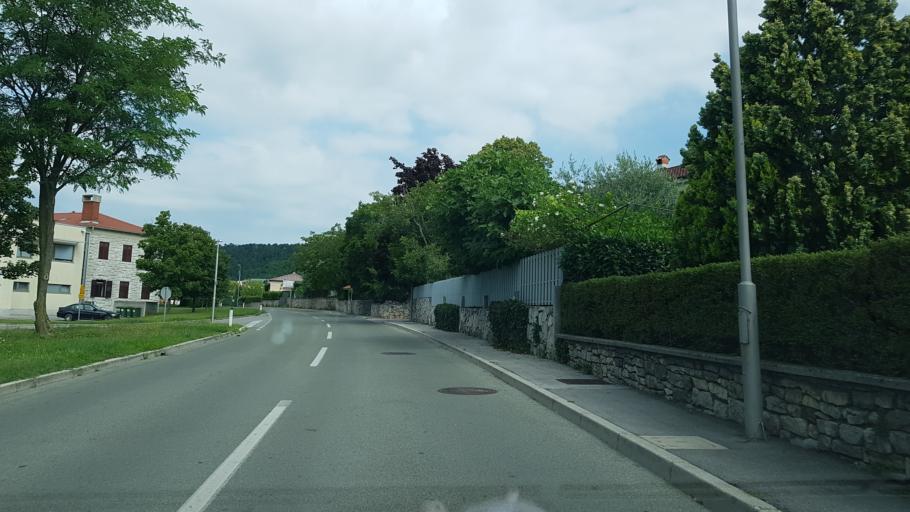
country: SI
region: Sezana
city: Sezana
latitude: 45.7015
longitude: 13.8727
